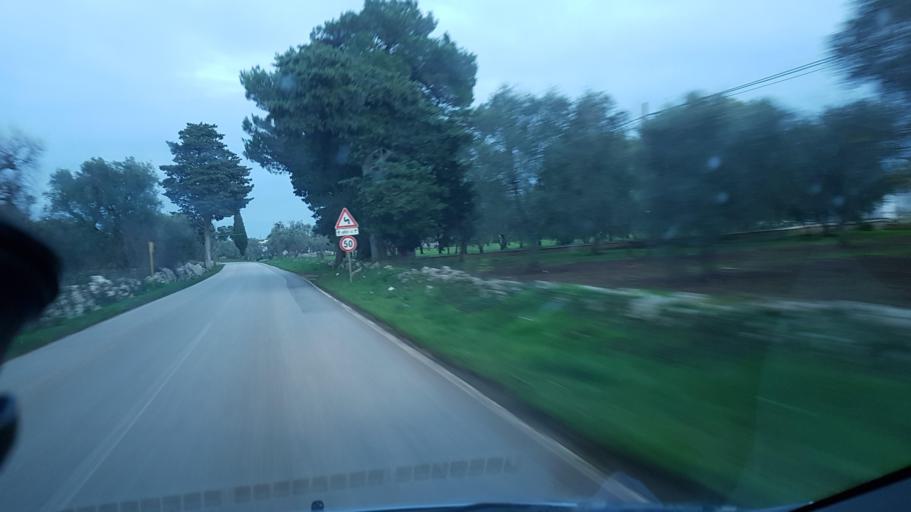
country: IT
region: Apulia
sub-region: Provincia di Brindisi
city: Ceglie Messapica
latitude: 40.6436
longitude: 17.5438
